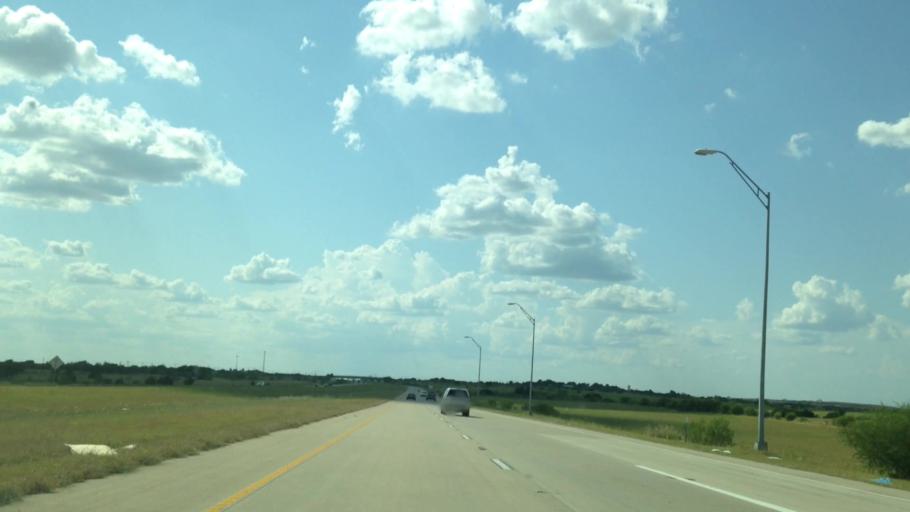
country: US
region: Texas
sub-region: Travis County
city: Onion Creek
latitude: 30.0858
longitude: -97.7394
